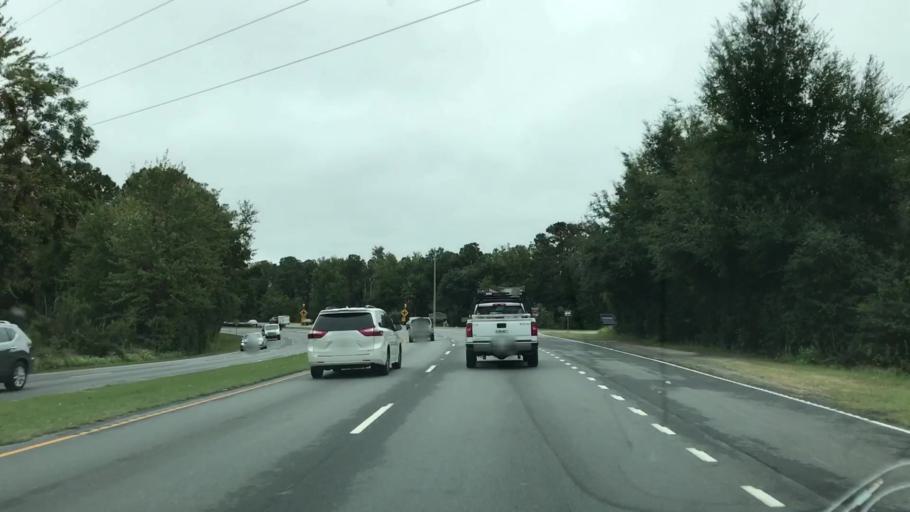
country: US
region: South Carolina
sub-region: Beaufort County
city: Hilton Head Island
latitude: 32.2197
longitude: -80.7772
